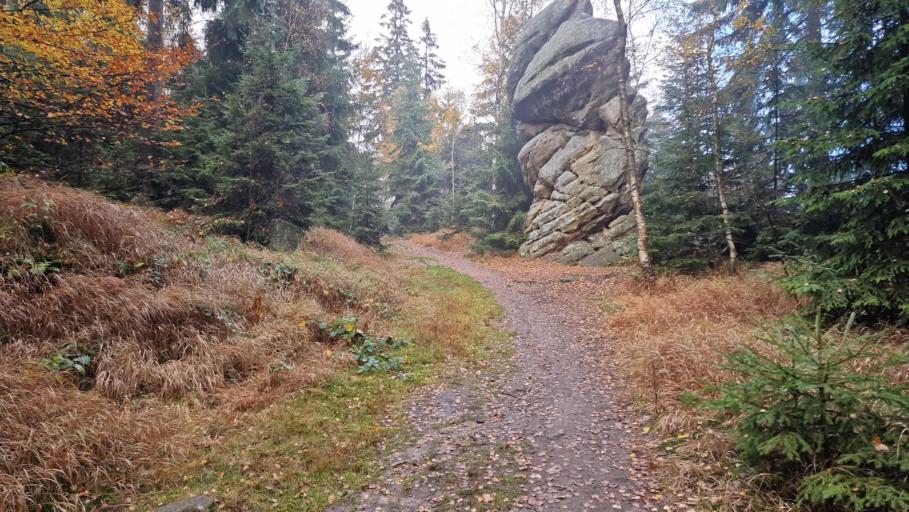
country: CZ
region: Kralovehradecky
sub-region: Okres Nachod
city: Police nad Metuji
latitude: 50.5581
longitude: 16.2822
